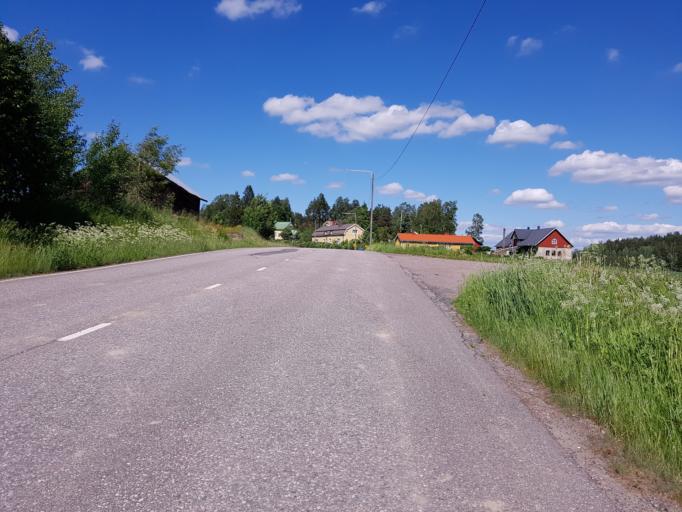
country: FI
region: Uusimaa
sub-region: Helsinki
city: Teekkarikylae
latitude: 60.2884
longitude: 24.8917
